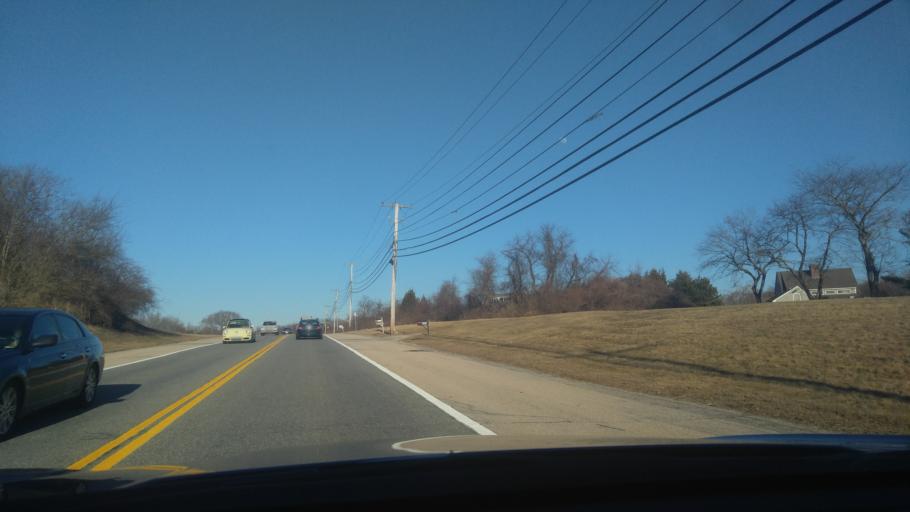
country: US
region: Rhode Island
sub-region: Washington County
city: Narragansett Pier
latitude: 41.4504
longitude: -71.4473
